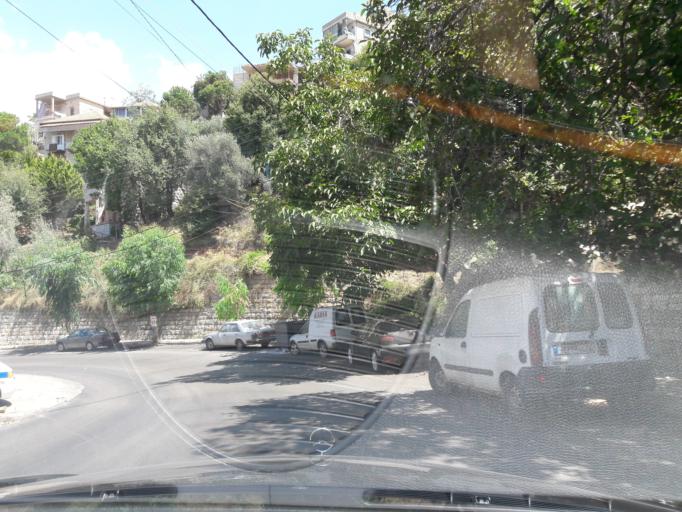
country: LB
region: Mont-Liban
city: Djounie
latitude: 33.9287
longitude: 35.6729
